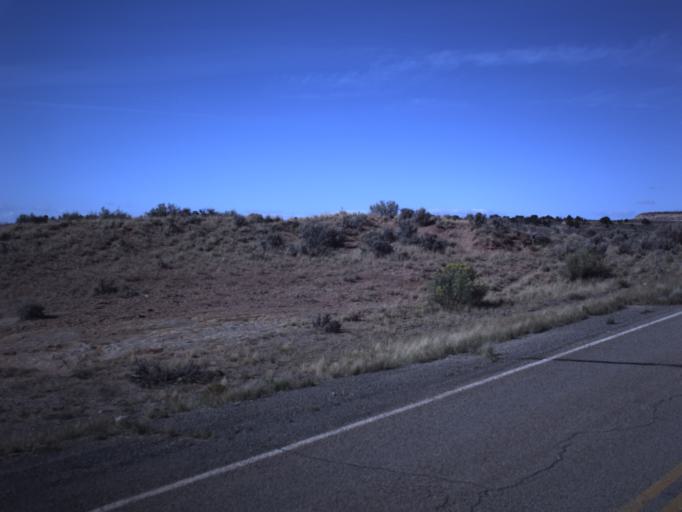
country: US
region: Utah
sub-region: San Juan County
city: Monticello
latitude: 38.0312
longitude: -109.4208
